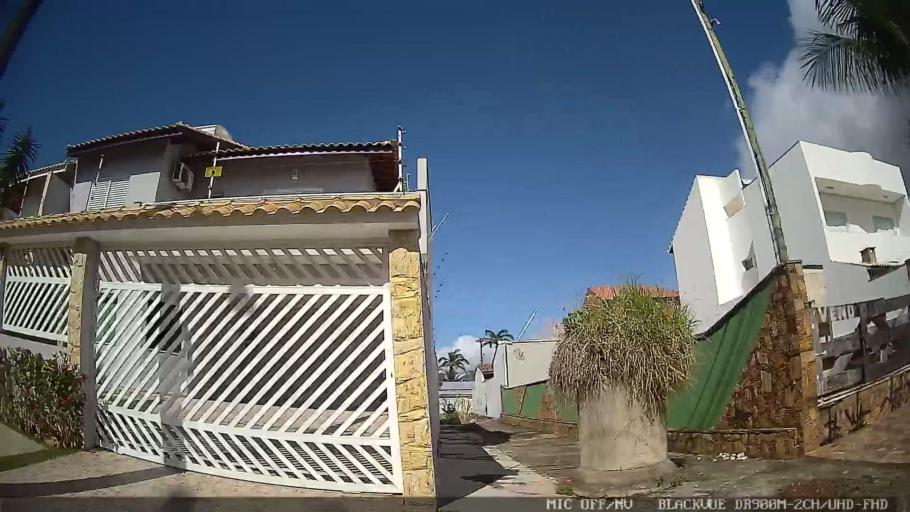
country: BR
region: Sao Paulo
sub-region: Peruibe
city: Peruibe
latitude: -24.2857
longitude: -46.9544
